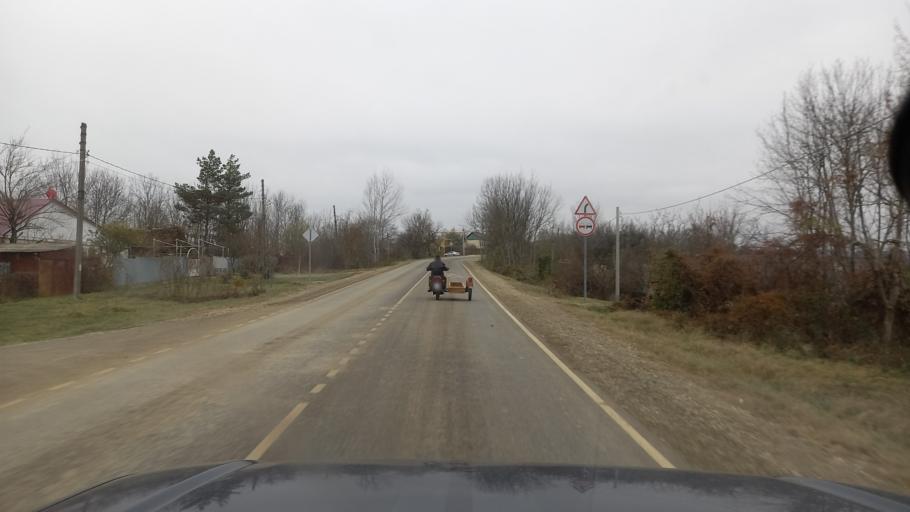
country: RU
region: Krasnodarskiy
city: Goryachiy Klyuch
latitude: 44.5243
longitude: 39.2927
